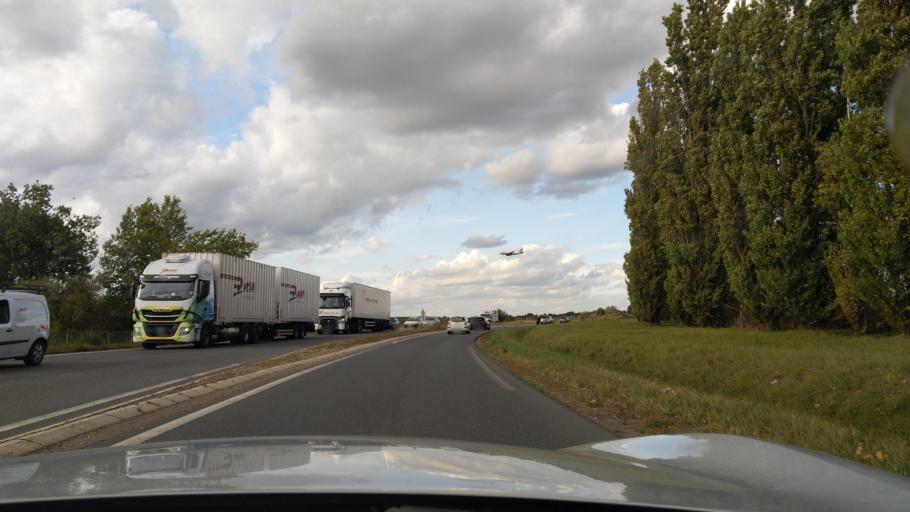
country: FR
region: Ile-de-France
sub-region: Departement de Seine-et-Marne
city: Mitry-Mory
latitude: 49.0192
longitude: 2.5835
